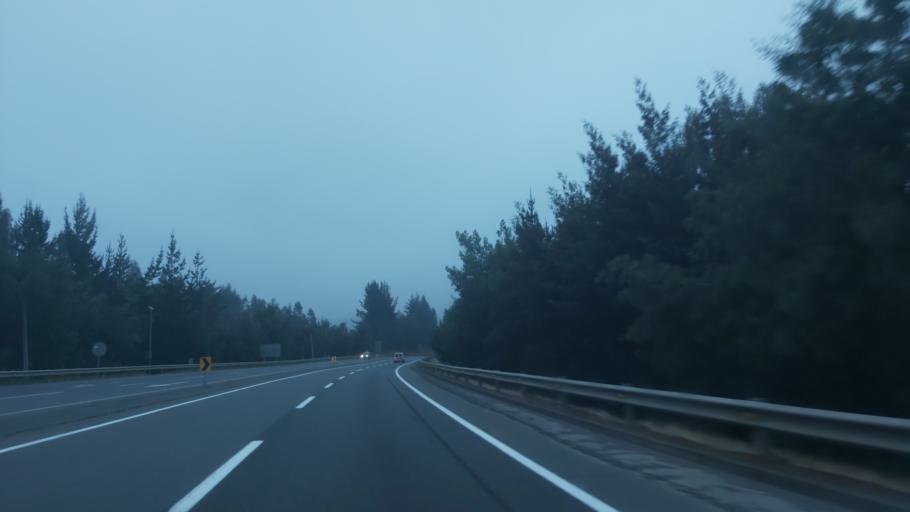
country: CL
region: Biobio
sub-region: Provincia de Concepcion
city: Penco
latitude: -36.7373
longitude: -72.8916
